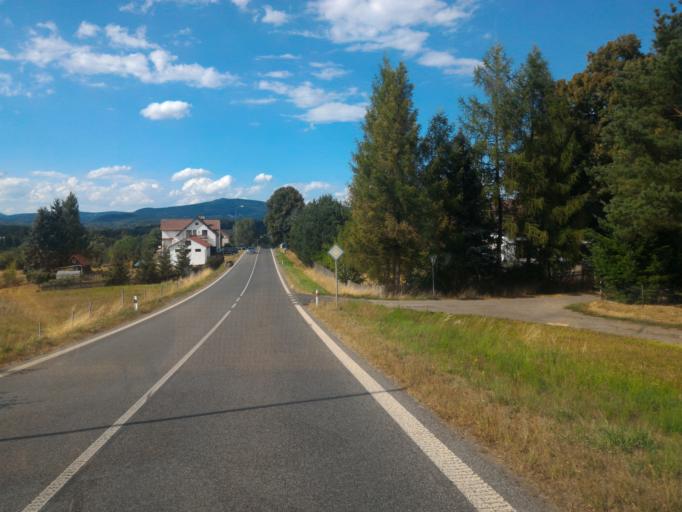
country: CZ
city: Jablonne v Podjestedi
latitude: 50.7570
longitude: 14.7605
